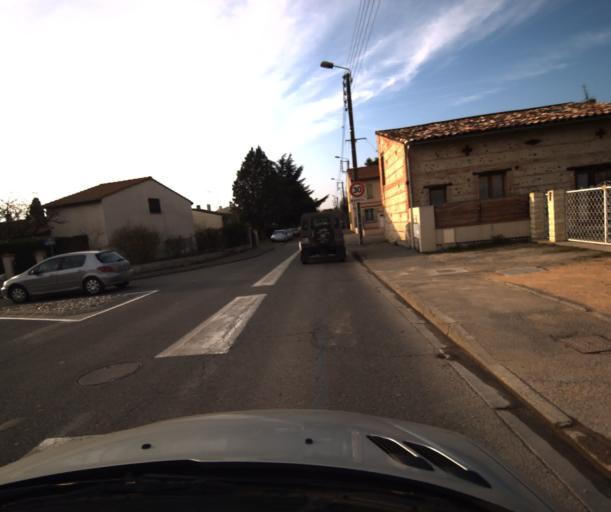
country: FR
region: Midi-Pyrenees
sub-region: Departement de la Haute-Garonne
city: Launaguet
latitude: 43.6771
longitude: 1.4558
